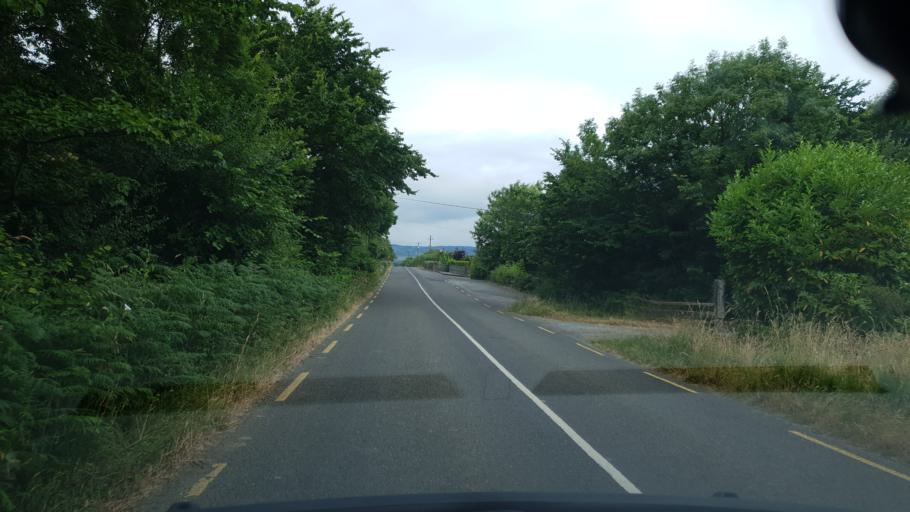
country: IE
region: Munster
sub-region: Ciarrai
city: Cill Airne
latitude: 52.1610
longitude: -9.6037
